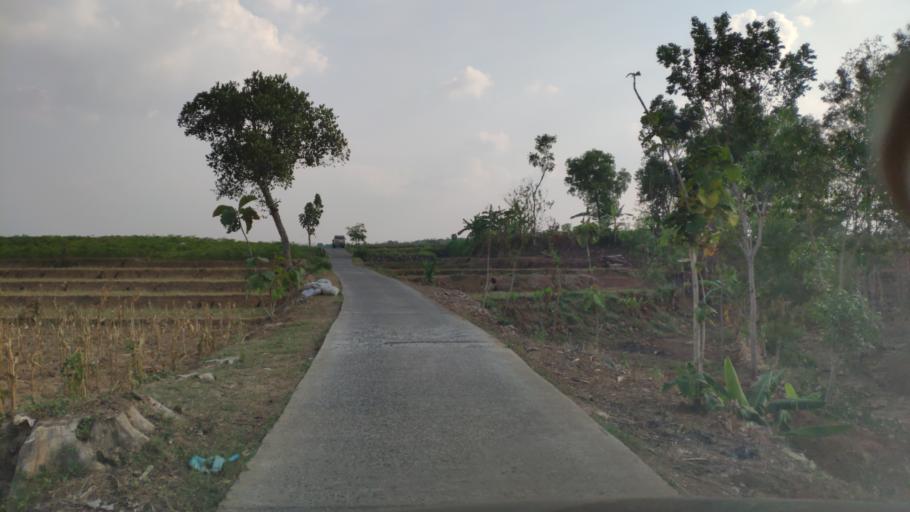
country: ID
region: Central Java
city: Guyangan
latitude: -6.9584
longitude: 111.1239
